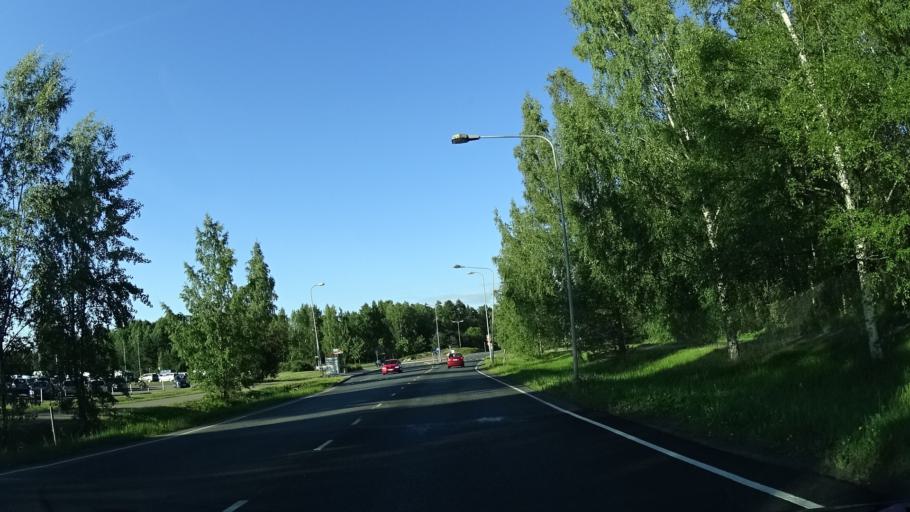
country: FI
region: Uusimaa
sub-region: Helsinki
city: Teekkarikylae
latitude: 60.2645
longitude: 24.8810
